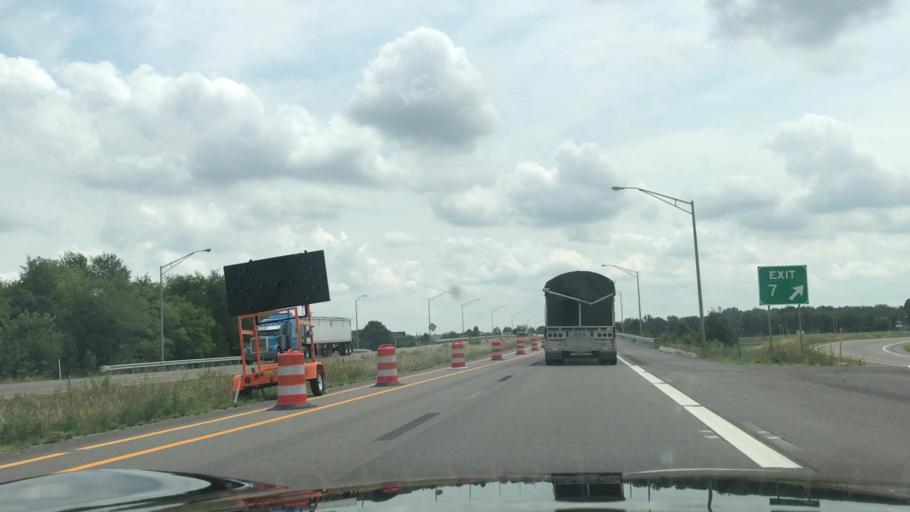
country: US
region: Kentucky
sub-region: Warren County
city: Bowling Green
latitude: 36.9606
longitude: -86.4978
